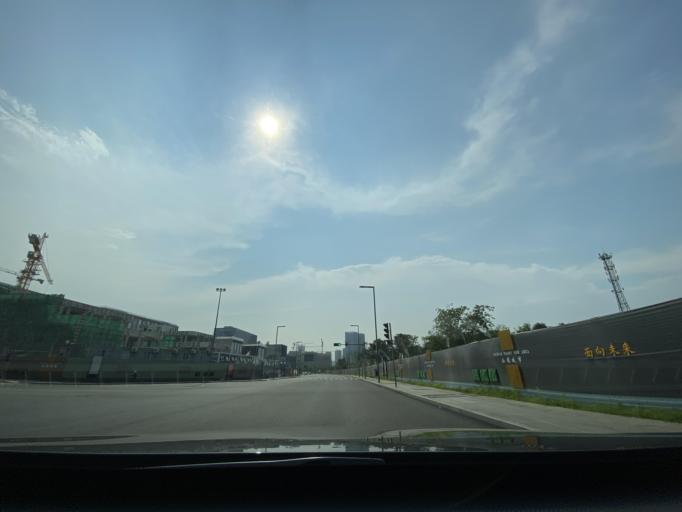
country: CN
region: Sichuan
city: Dongsheng
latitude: 30.3931
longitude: 104.0824
